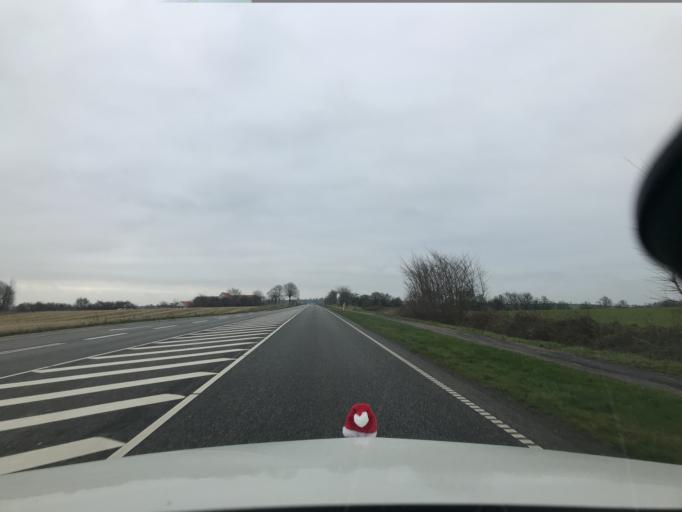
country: DK
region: South Denmark
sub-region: Sonderborg Kommune
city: Dybbol
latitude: 54.9089
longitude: 9.7220
